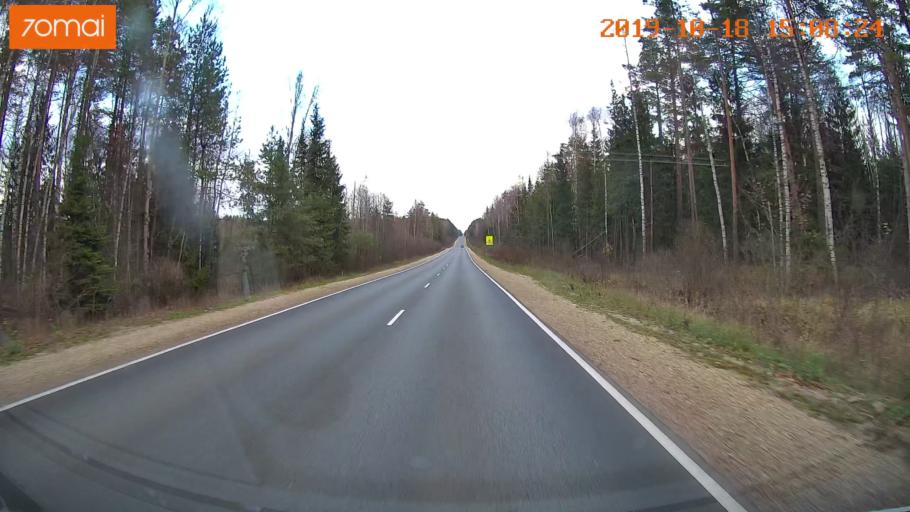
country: RU
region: Vladimir
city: Gus'-Khrustal'nyy
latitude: 55.5518
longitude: 40.6101
